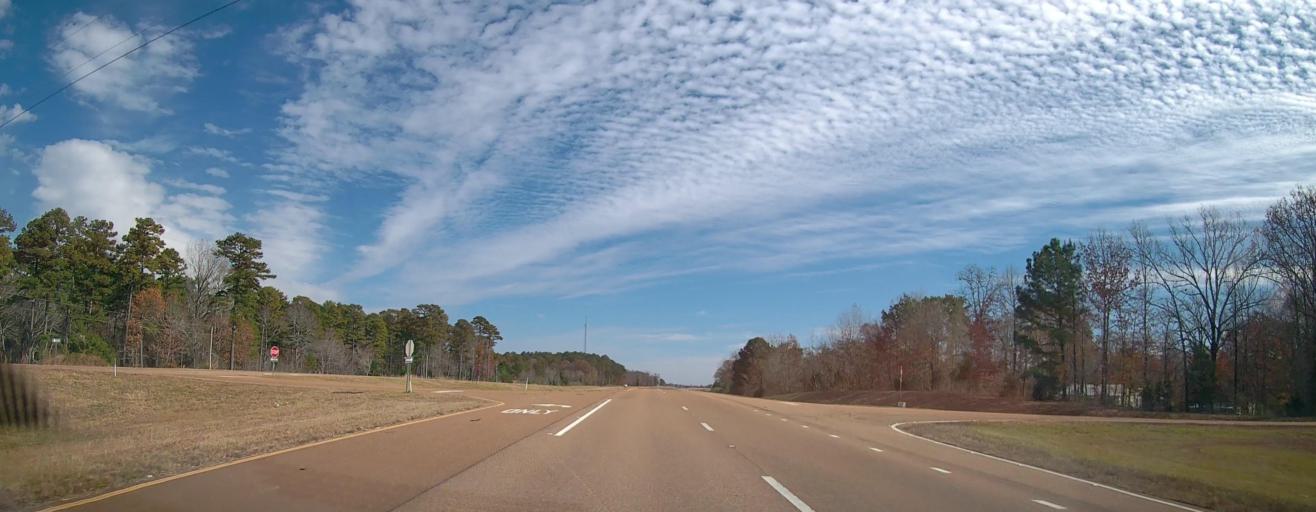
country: US
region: Mississippi
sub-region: Benton County
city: Ashland
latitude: 34.9544
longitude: -89.0264
